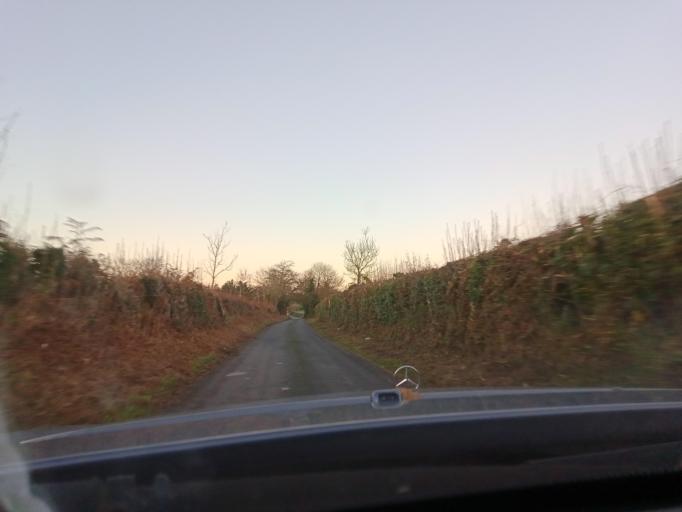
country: IE
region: Leinster
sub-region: Kilkenny
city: Thomastown
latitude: 52.4454
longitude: -7.1051
